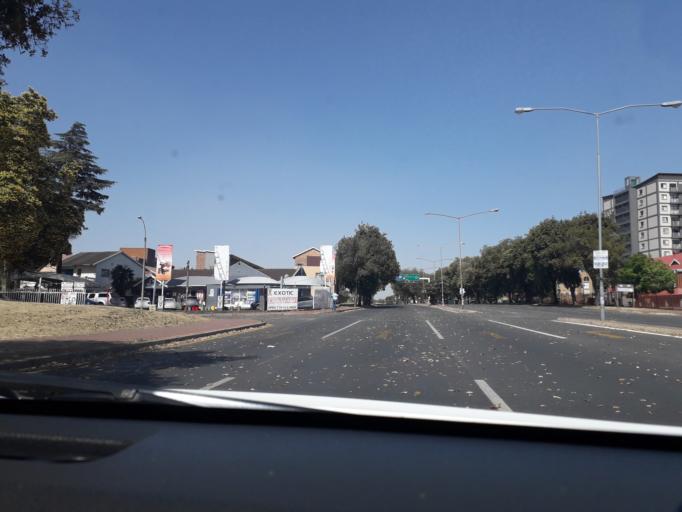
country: ZA
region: Gauteng
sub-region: City of Johannesburg Metropolitan Municipality
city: Modderfontein
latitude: -26.1017
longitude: 28.2294
